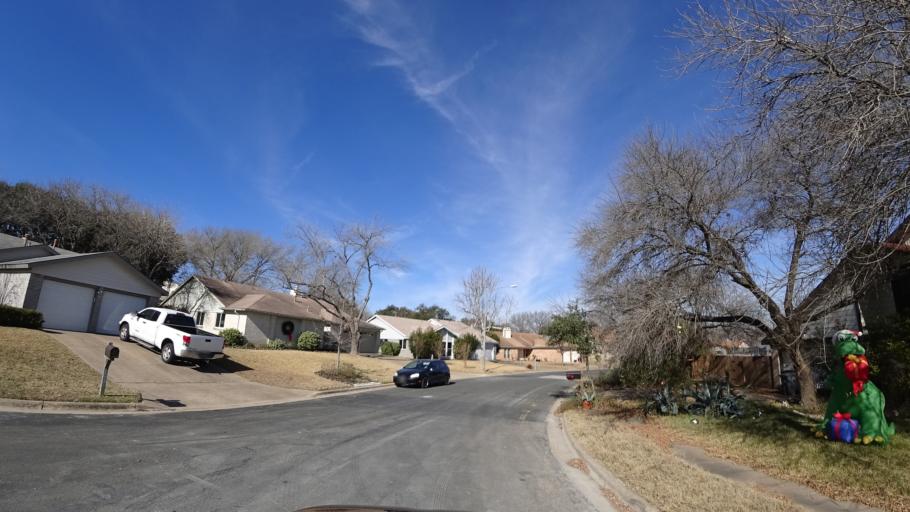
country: US
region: Texas
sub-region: Travis County
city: Wells Branch
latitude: 30.3912
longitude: -97.6906
